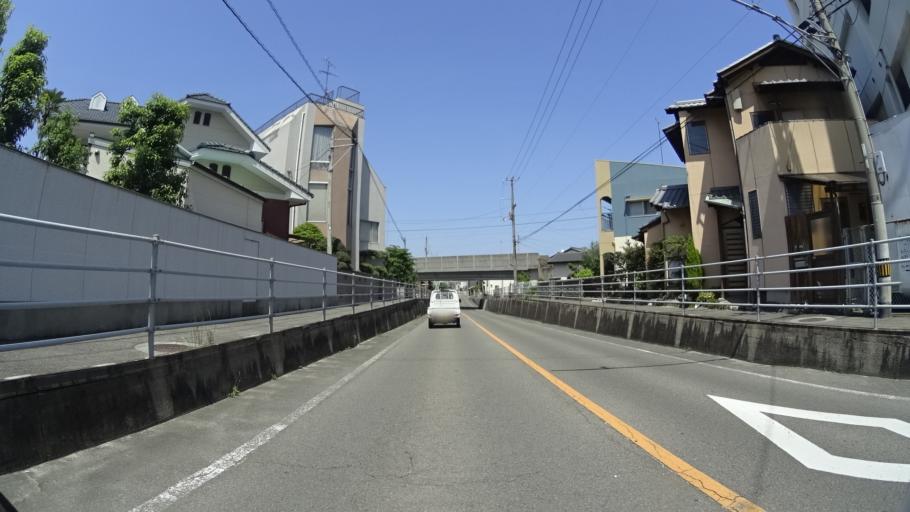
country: JP
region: Ehime
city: Saijo
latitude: 34.0561
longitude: 132.9984
